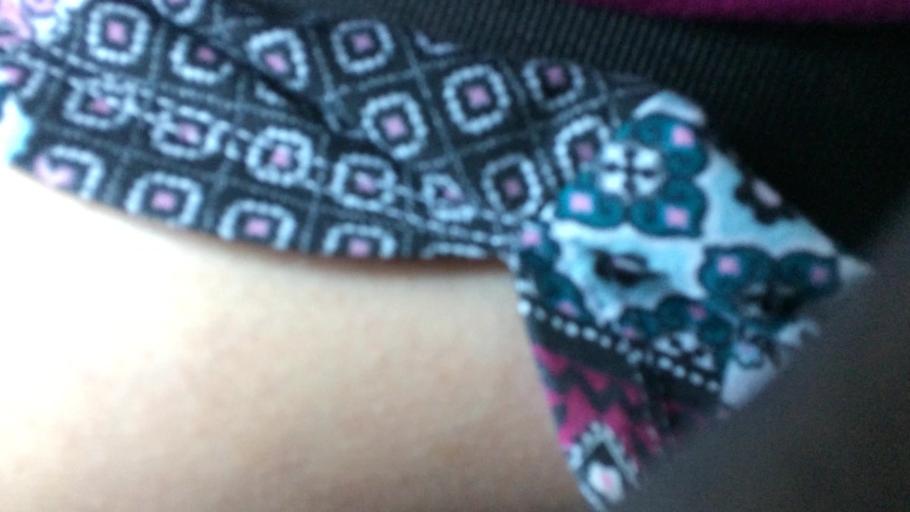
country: US
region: New Mexico
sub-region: Colfax County
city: Springer
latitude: 35.9684
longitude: -104.7549
